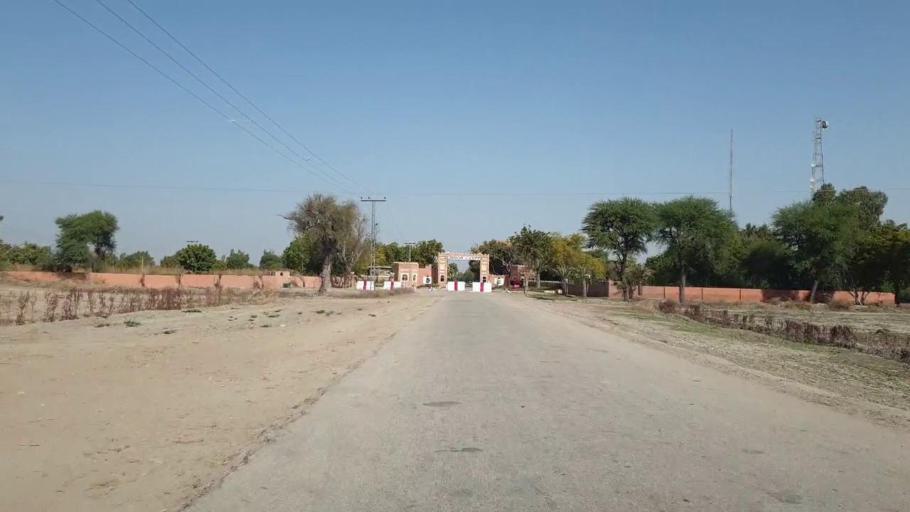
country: PK
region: Sindh
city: Chor
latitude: 25.5017
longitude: 69.7792
